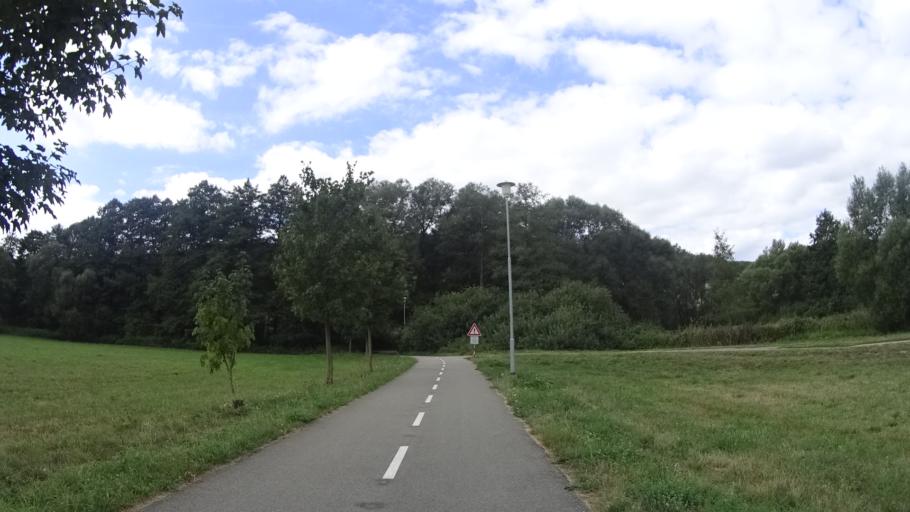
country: CZ
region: Pardubicky
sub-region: Okres Usti nad Orlici
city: Usti nad Orlici
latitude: 49.9810
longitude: 16.3872
